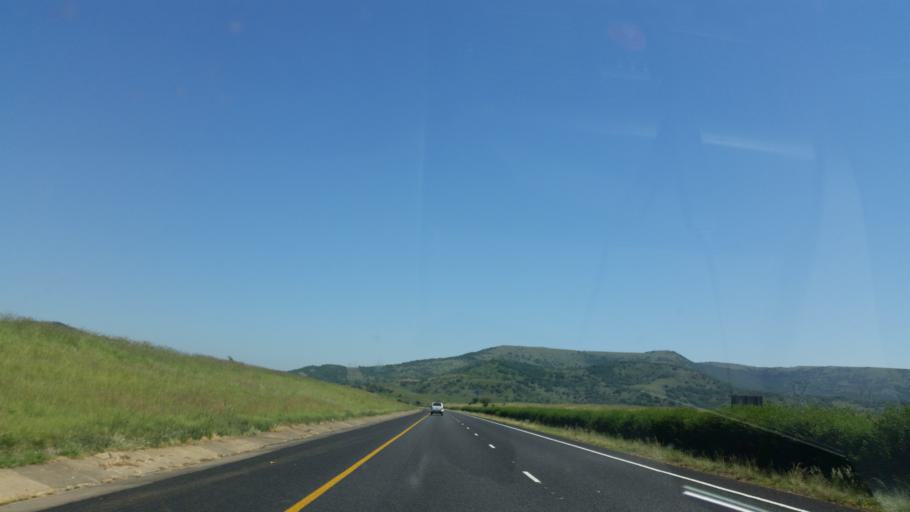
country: ZA
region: KwaZulu-Natal
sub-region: uThukela District Municipality
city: Ladysmith
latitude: -28.7658
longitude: 29.6717
